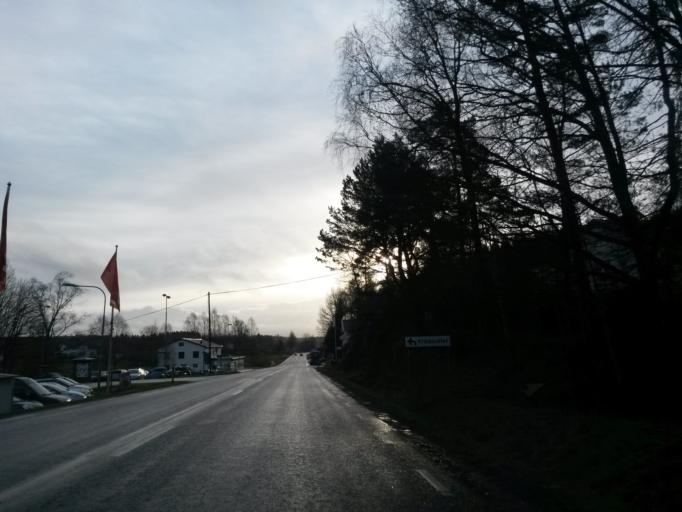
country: SE
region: Vaestra Goetaland
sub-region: Harryda Kommun
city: Ravlanda
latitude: 57.5494
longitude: 12.5313
